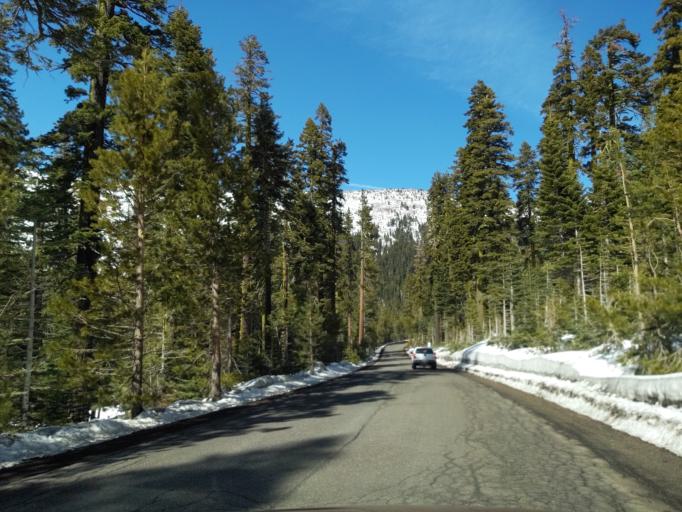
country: US
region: California
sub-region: El Dorado County
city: South Lake Tahoe
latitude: 38.8109
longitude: -120.0810
